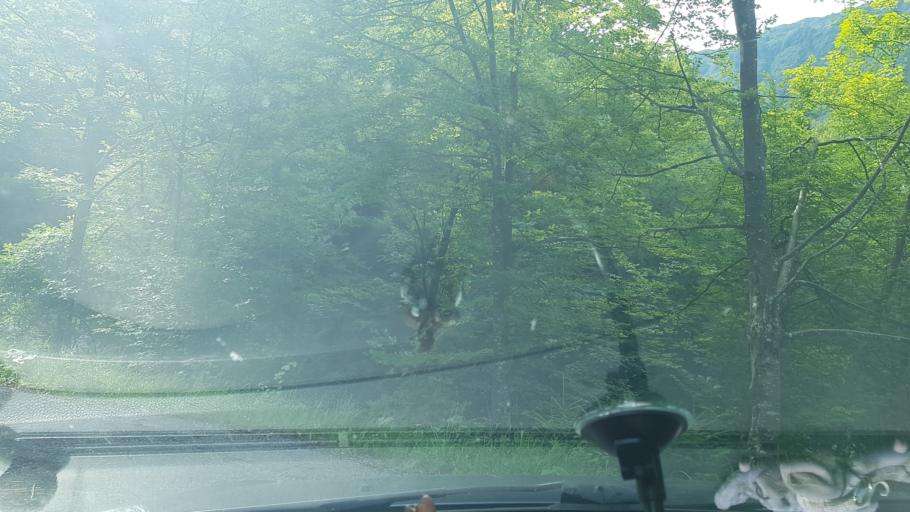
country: IT
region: Friuli Venezia Giulia
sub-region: Provincia di Udine
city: Prato
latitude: 46.3399
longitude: 13.4096
